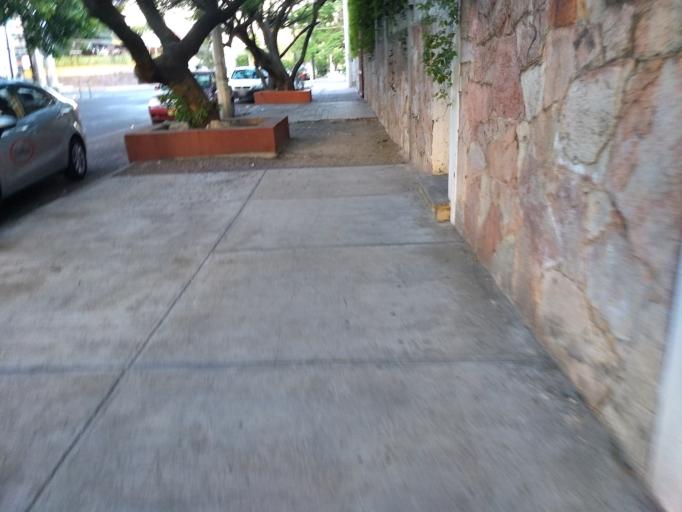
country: MX
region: Jalisco
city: Guadalajara
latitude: 20.6720
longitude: -103.3819
